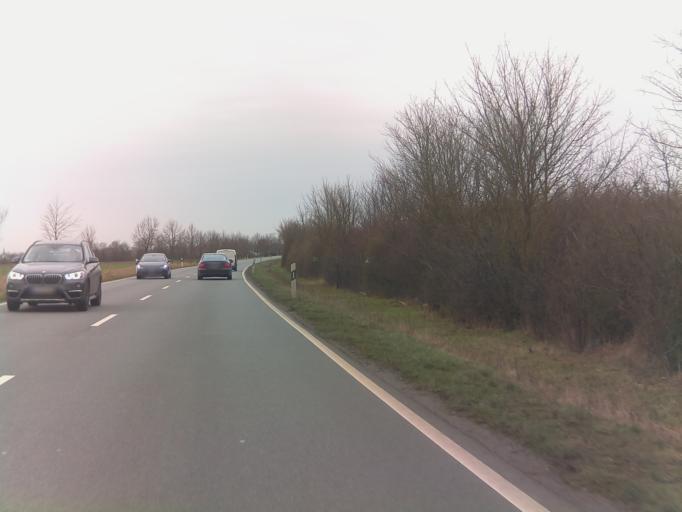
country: DE
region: Hesse
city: Biebesheim
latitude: 49.7886
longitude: 8.4863
